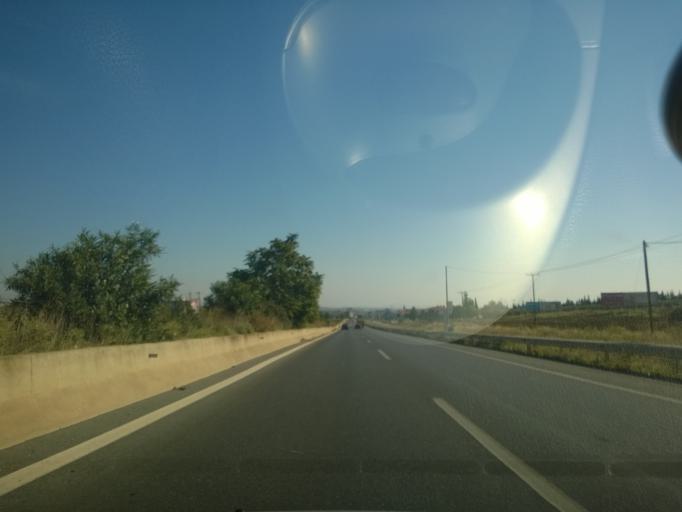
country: GR
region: Central Macedonia
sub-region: Nomos Thessalonikis
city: Kato Scholari
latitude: 40.4357
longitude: 23.0154
